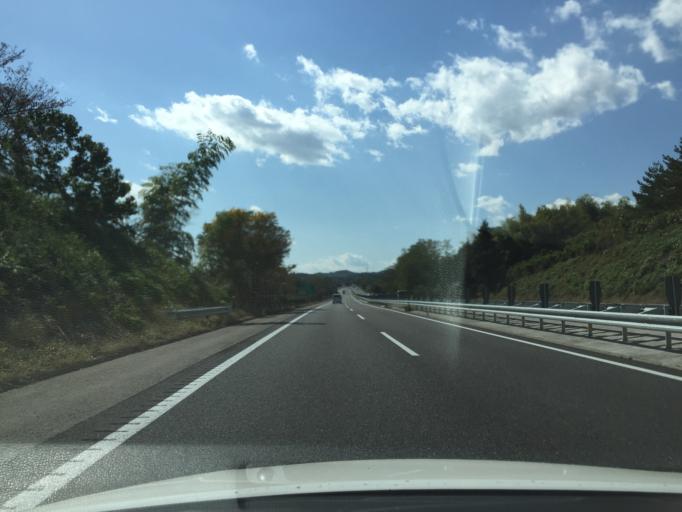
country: JP
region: Fukushima
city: Sukagawa
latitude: 37.2020
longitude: 140.3043
